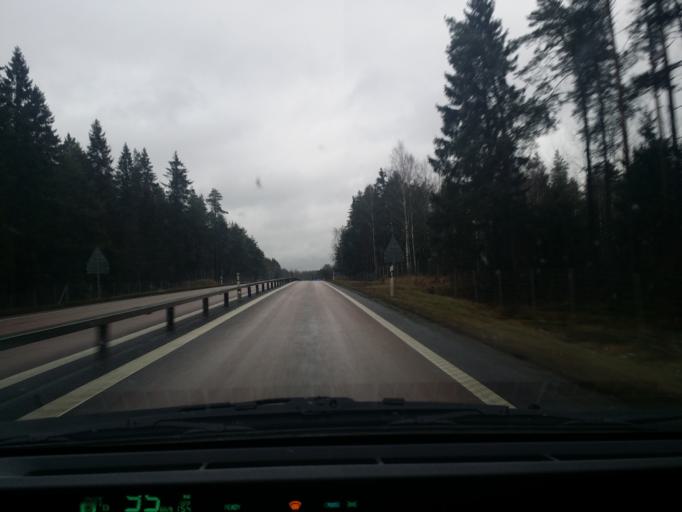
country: SE
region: Vaestmanland
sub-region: Sala Kommun
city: Sala
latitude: 59.8823
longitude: 16.5507
